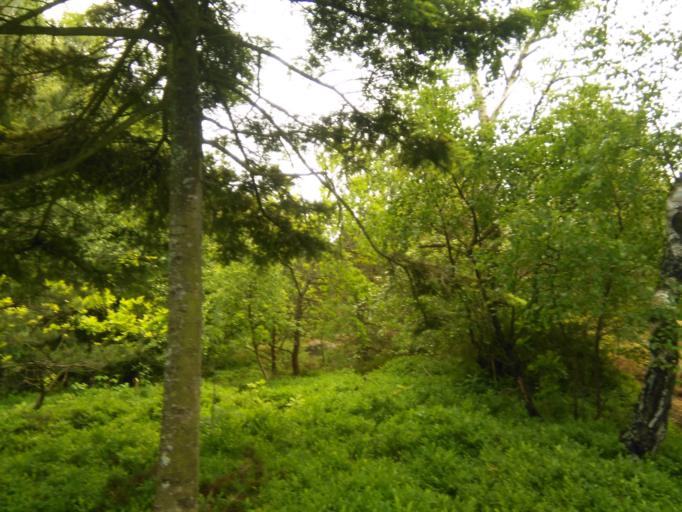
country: DK
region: Capital Region
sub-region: Bornholm Kommune
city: Nexo
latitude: 55.0917
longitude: 15.1062
